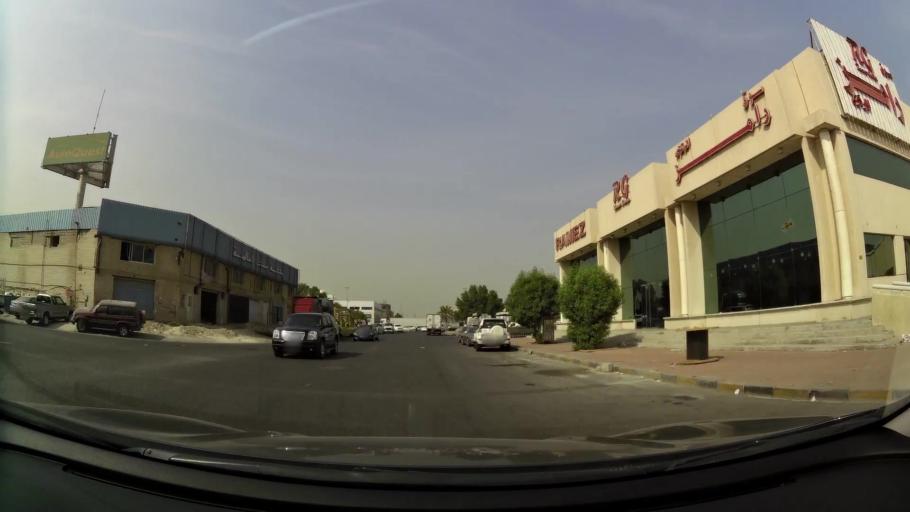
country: KW
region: Al Asimah
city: Ar Rabiyah
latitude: 29.3210
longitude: 47.9340
